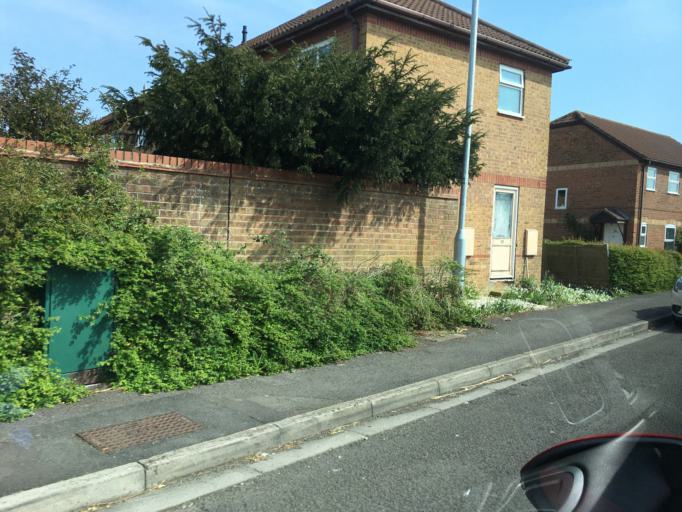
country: GB
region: England
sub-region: South Gloucestershire
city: Almondsbury
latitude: 51.5432
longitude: -2.5506
